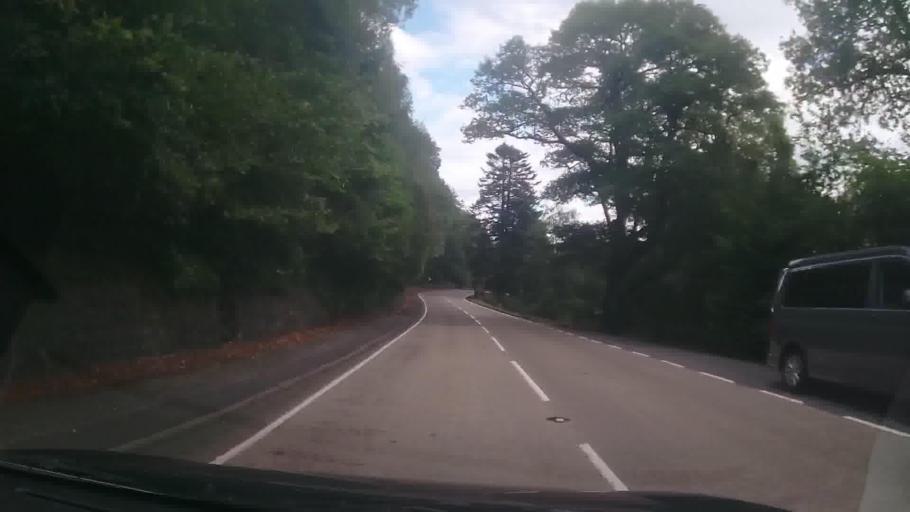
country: GB
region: Scotland
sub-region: Argyll and Bute
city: Garelochhead
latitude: 56.3954
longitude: -5.0570
